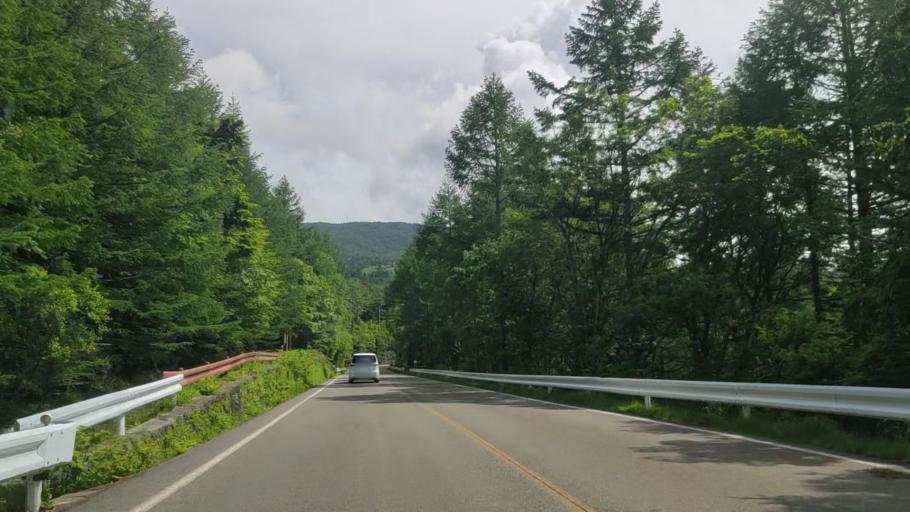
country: JP
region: Yamanashi
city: Fujikawaguchiko
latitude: 35.4124
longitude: 138.6997
